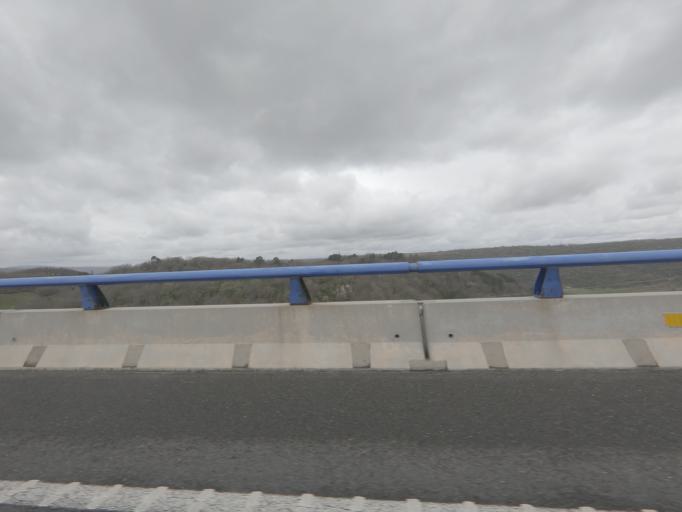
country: ES
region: Castille and Leon
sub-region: Provincia de Salamanca
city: Puerto de Bejar
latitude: 40.3586
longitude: -5.8387
